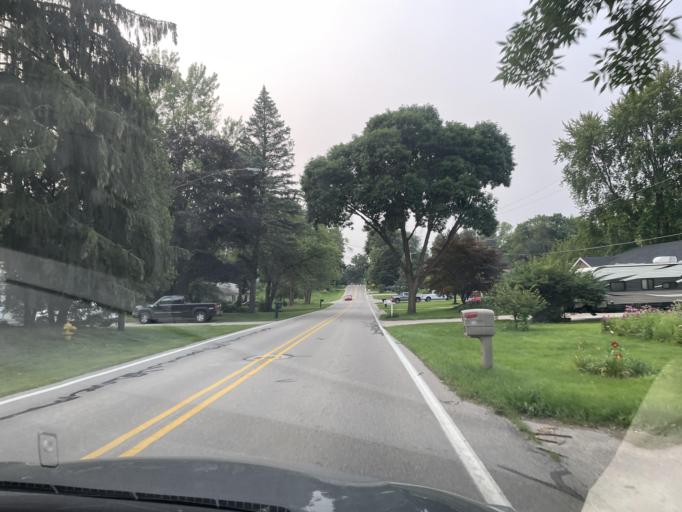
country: US
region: Michigan
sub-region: Kent County
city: Walker
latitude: 42.9679
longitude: -85.7370
